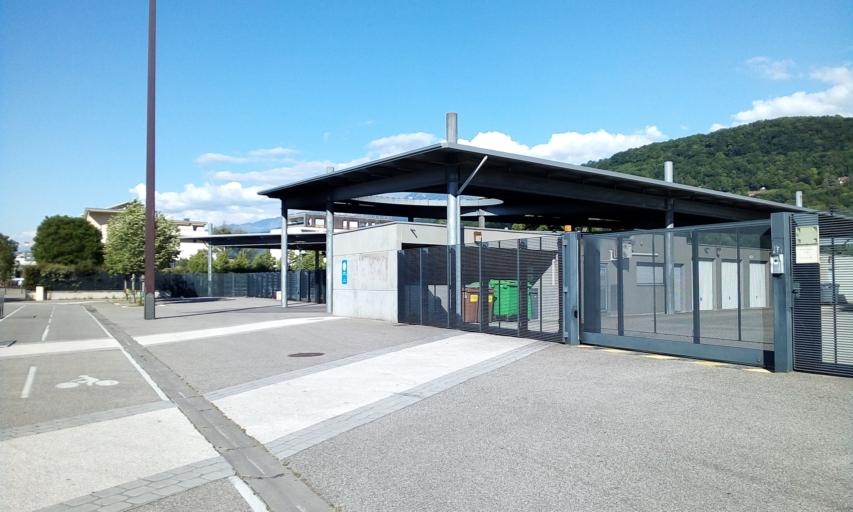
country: FR
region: Rhone-Alpes
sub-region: Departement de l'Isere
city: Saint-Martin-d'Heres
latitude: 45.1740
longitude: 5.7614
